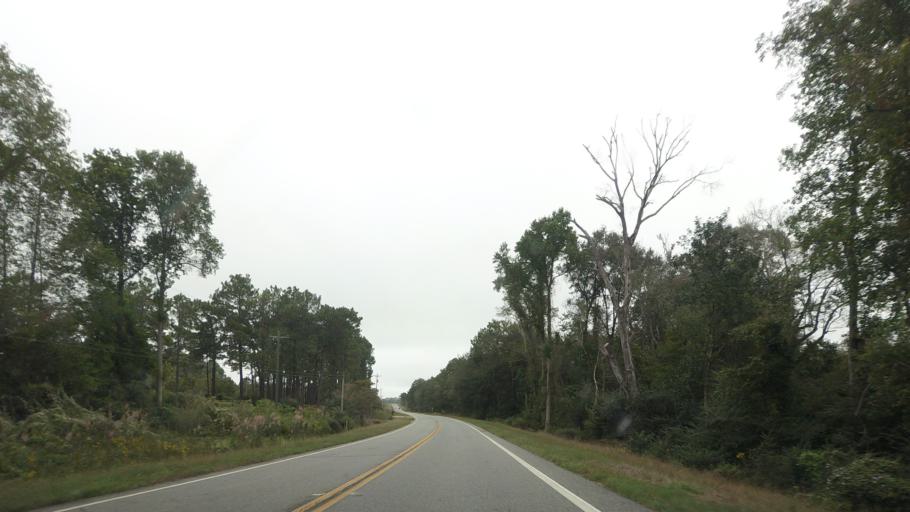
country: US
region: Georgia
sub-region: Irwin County
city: Ocilla
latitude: 31.5118
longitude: -83.2393
